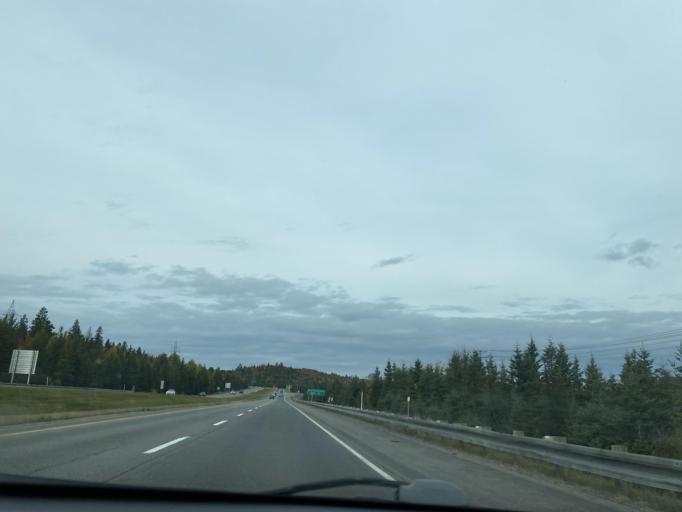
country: CA
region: Quebec
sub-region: Laurentides
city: Sainte-Agathe-des-Monts
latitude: 46.0533
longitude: -74.2702
